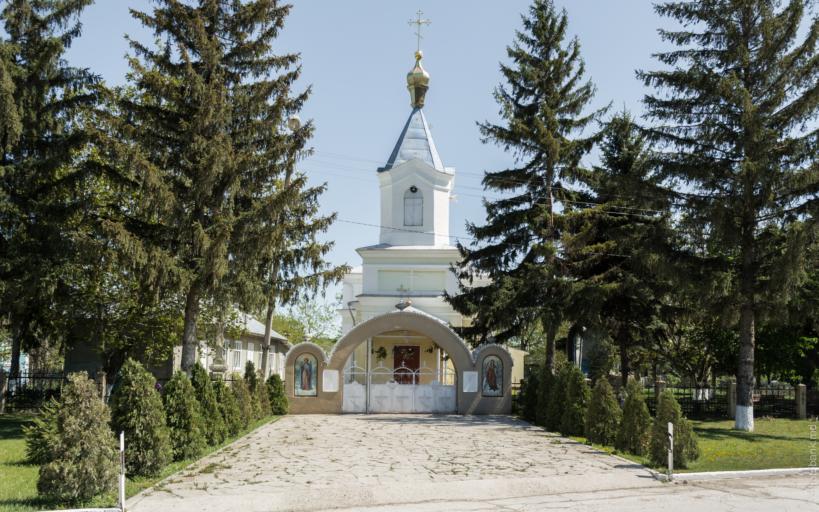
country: MD
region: Balti
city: Balti
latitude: 47.8300
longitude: 27.8372
